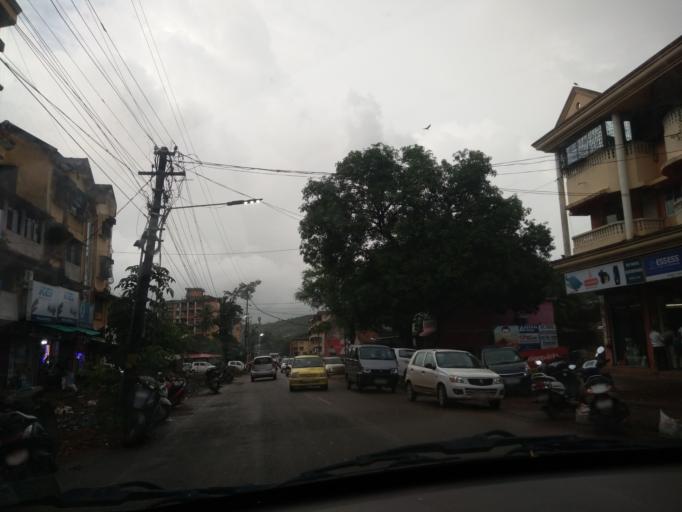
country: IN
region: Goa
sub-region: South Goa
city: Raia
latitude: 15.2962
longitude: 73.9695
